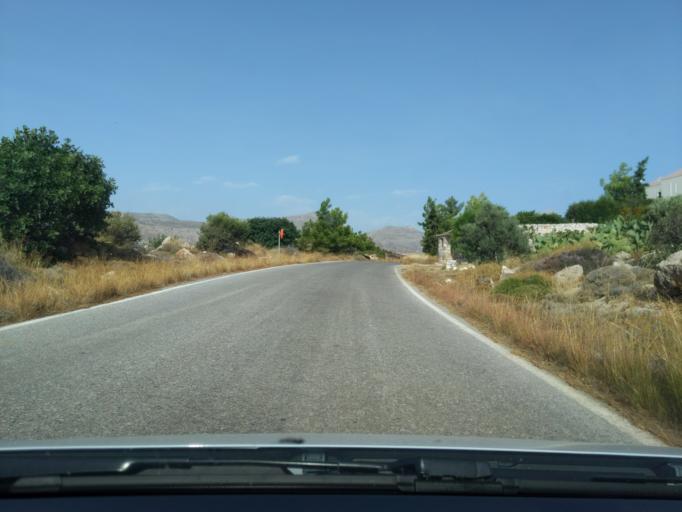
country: GR
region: Crete
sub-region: Nomos Lasithiou
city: Palekastro
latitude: 35.0852
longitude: 26.2448
